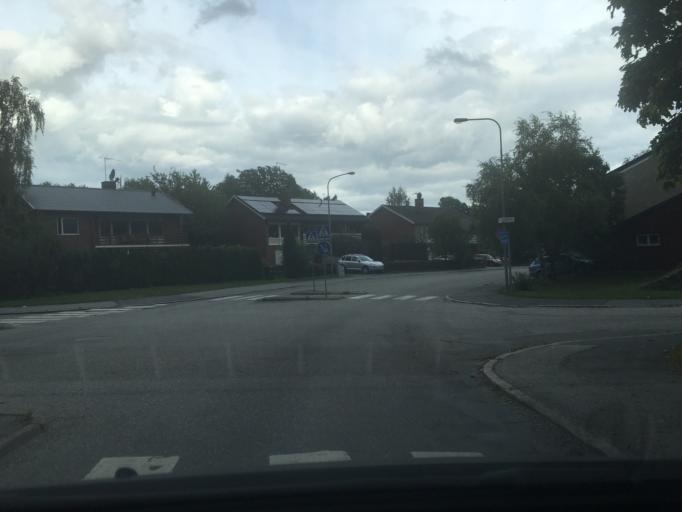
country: SE
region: Stockholm
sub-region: Stockholms Kommun
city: Bromma
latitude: 59.3716
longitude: 17.8861
